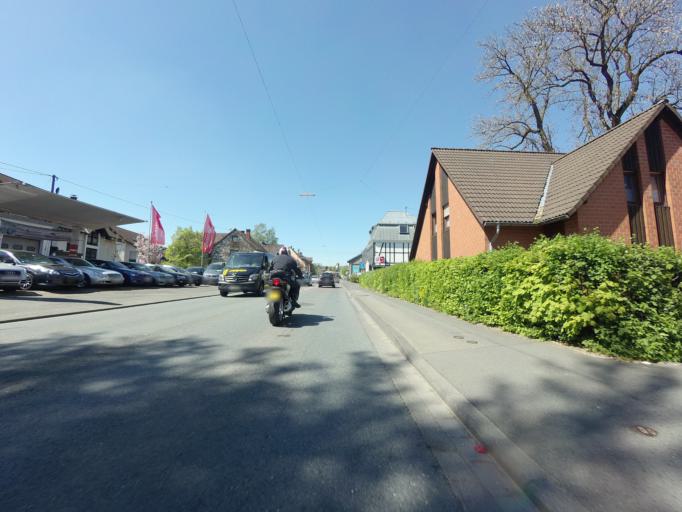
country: DE
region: North Rhine-Westphalia
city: Kreuztal
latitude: 50.9616
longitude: 8.0013
